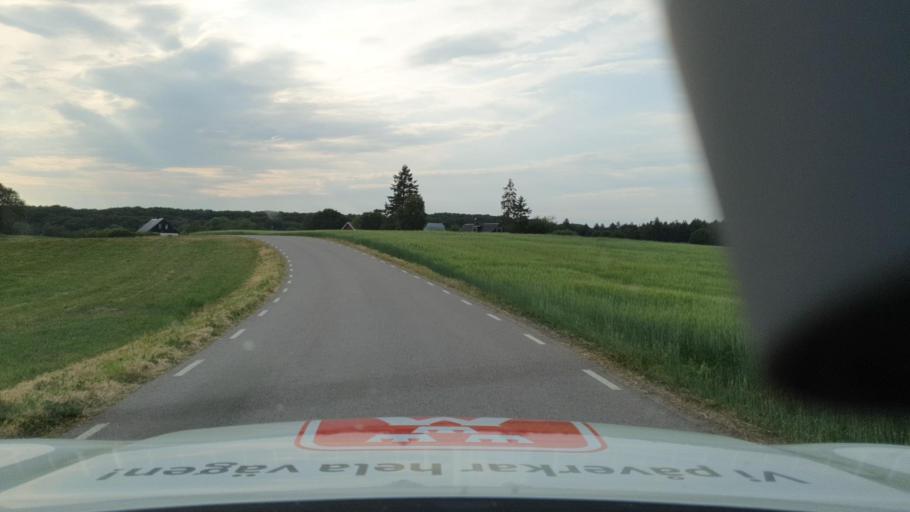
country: SE
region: Skane
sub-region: Tomelilla Kommun
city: Tomelilla
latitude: 55.6449
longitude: 13.8763
